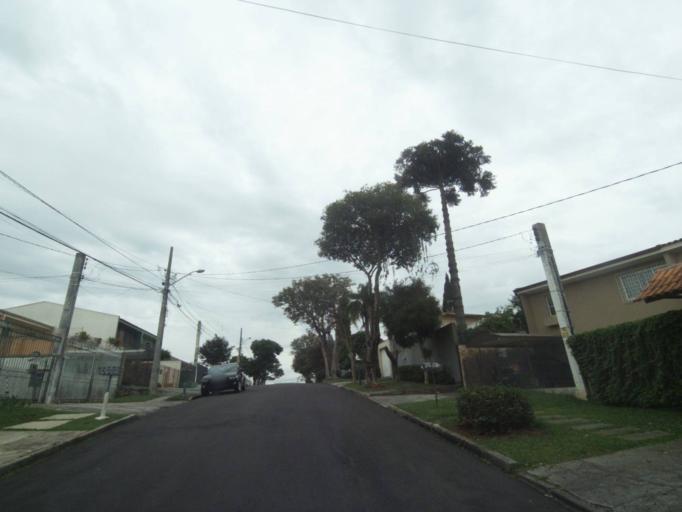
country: BR
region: Parana
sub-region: Curitiba
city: Curitiba
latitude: -25.3947
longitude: -49.2934
